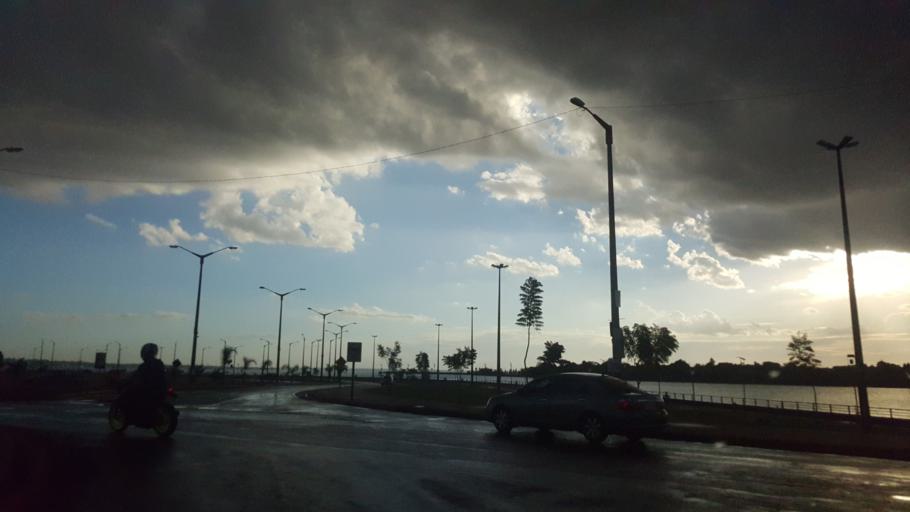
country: PY
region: Itapua
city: Encarnacion
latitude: -27.3214
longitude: -55.8737
